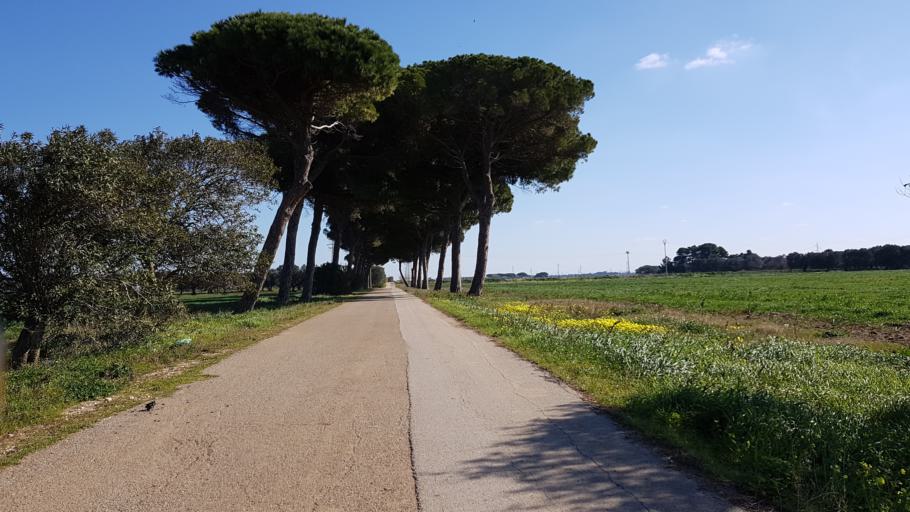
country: IT
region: Apulia
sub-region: Provincia di Brindisi
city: Mesagne
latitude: 40.6197
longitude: 17.8536
